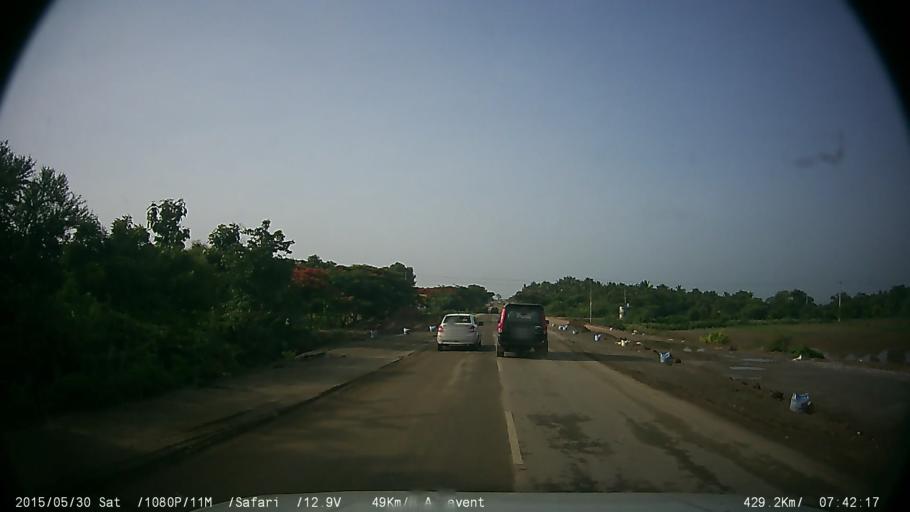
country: IN
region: Karnataka
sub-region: Chamrajnagar
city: Gundlupet
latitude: 11.9180
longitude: 76.6706
